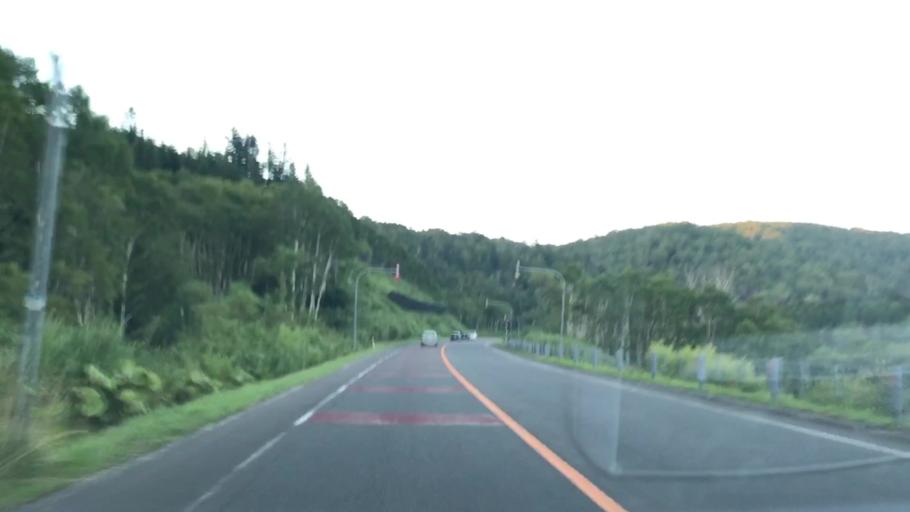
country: JP
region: Hokkaido
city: Sapporo
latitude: 42.8681
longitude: 141.1112
